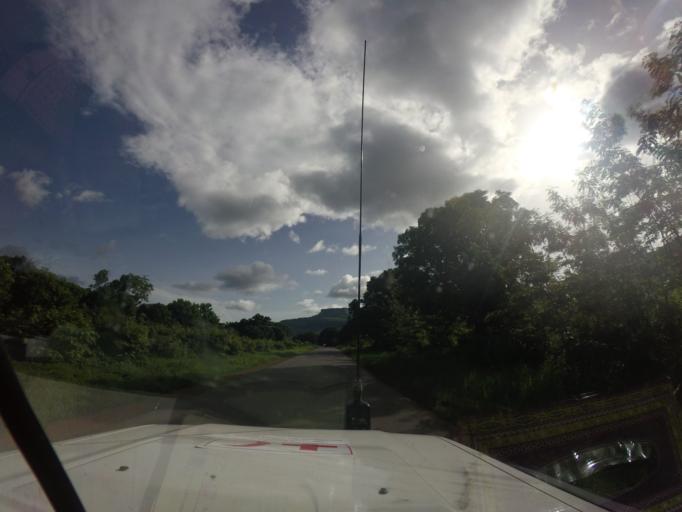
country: GN
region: Kindia
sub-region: Kindia
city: Kindia
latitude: 10.1709
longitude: -12.5209
